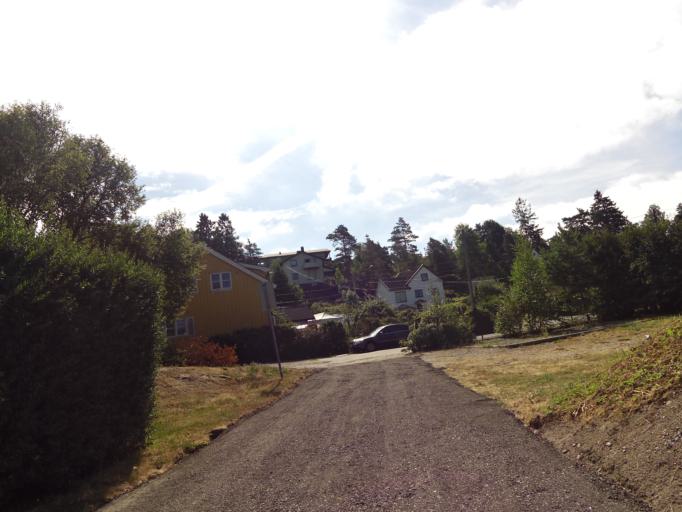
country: NO
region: Ostfold
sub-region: Fredrikstad
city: Fredrikstad
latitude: 59.2359
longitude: 10.9160
